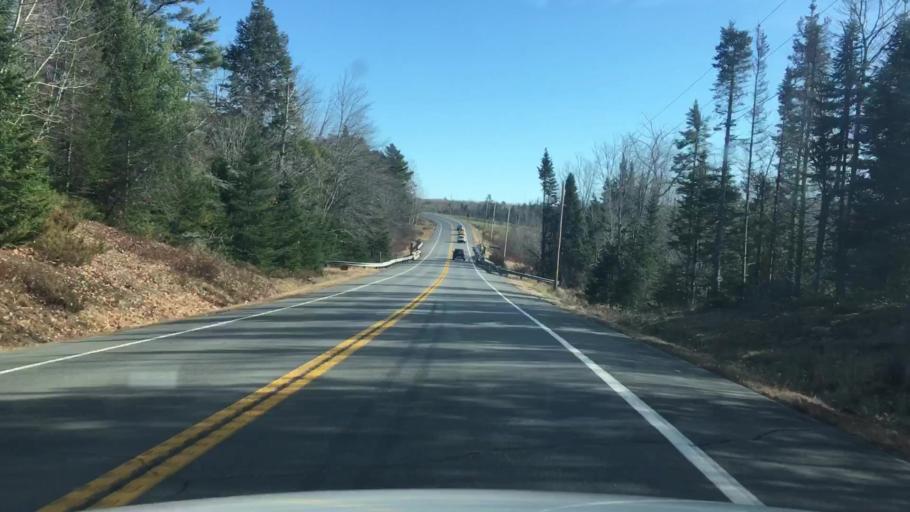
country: US
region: Maine
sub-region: Lincoln County
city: Jefferson
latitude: 44.2519
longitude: -69.4302
